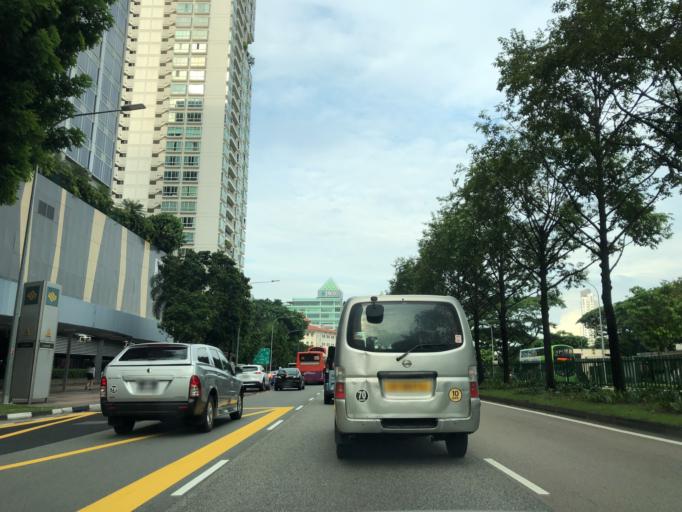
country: SG
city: Singapore
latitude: 1.3072
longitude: 103.8625
